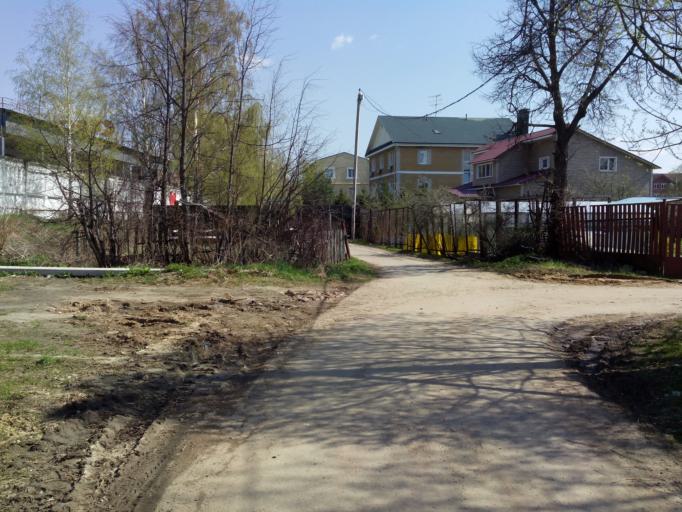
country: RU
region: Moskovskaya
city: Lesnoy Gorodok
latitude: 55.6630
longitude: 37.2353
